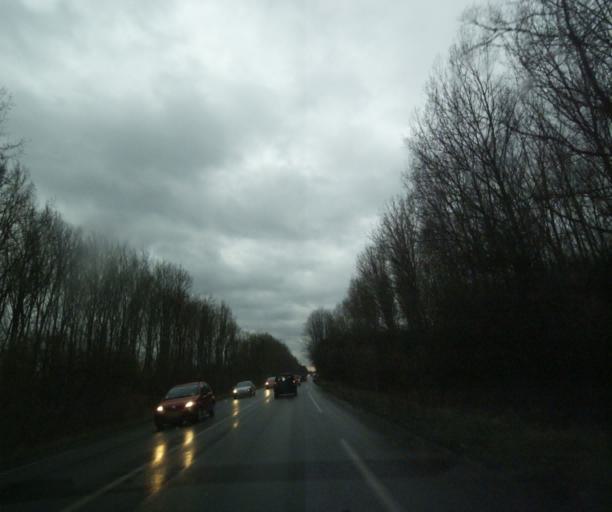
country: FR
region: Nord-Pas-de-Calais
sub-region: Departement du Nord
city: Vicq
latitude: 50.4057
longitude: 3.5813
